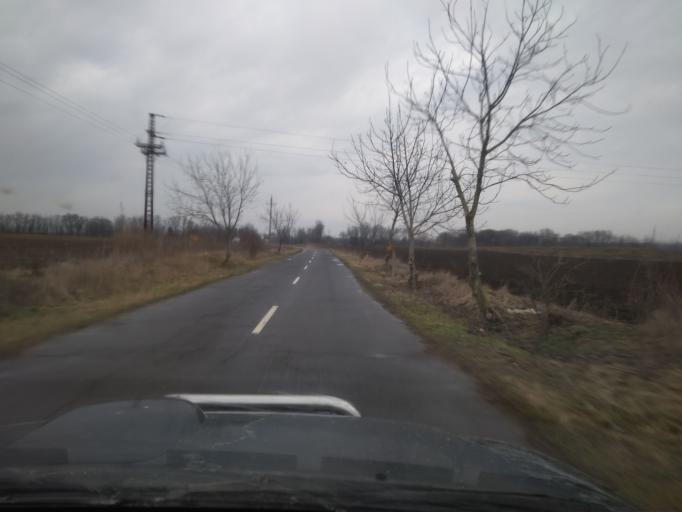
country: HU
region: Szabolcs-Szatmar-Bereg
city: Nyirtelek
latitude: 47.9646
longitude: 21.6472
